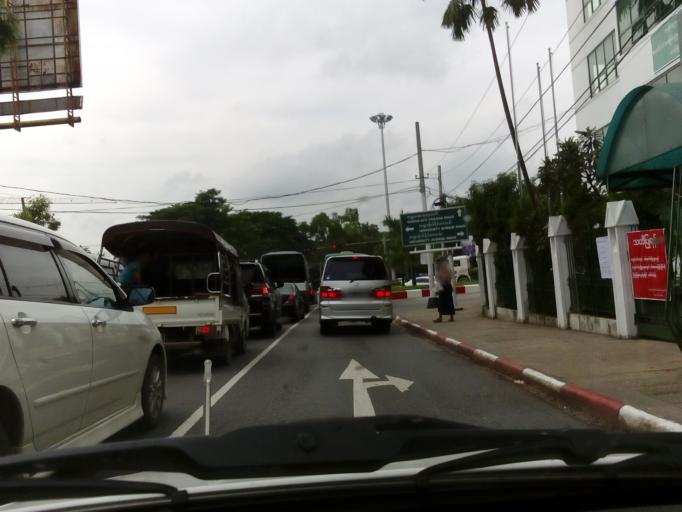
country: MM
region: Yangon
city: Yangon
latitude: 16.8227
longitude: 96.1542
